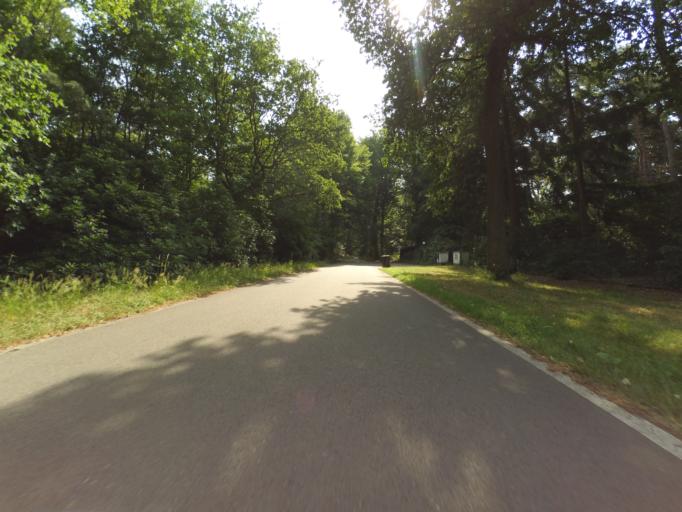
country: BE
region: Flanders
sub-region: Provincie Antwerpen
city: Stabroek
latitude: 51.3549
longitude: 4.3775
